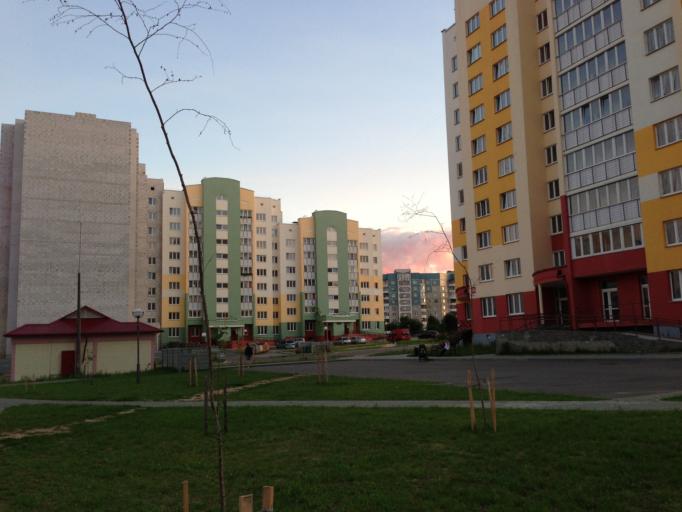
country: BY
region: Grodnenskaya
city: Hrodna
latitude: 53.7072
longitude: 23.8573
